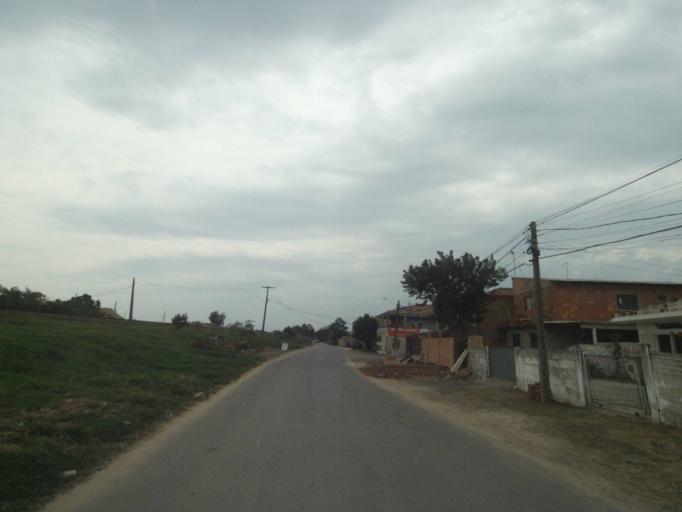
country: BR
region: Parana
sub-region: Sao Jose Dos Pinhais
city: Sao Jose dos Pinhais
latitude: -25.4967
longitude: -49.2052
